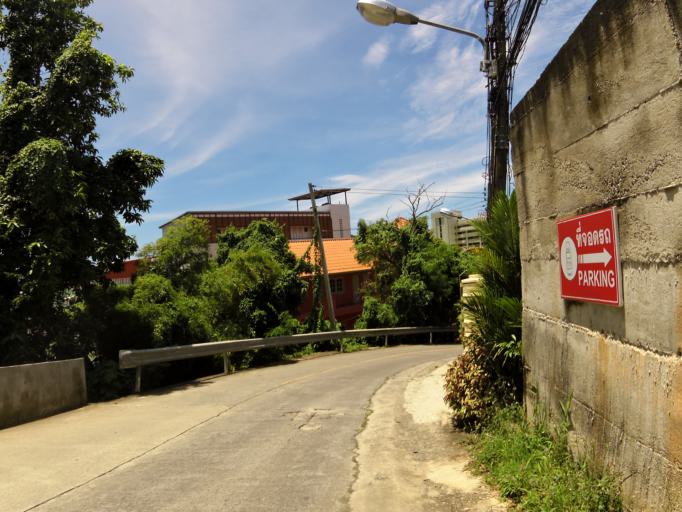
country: TH
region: Phuket
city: Ban Karon
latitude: 7.8474
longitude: 98.2991
